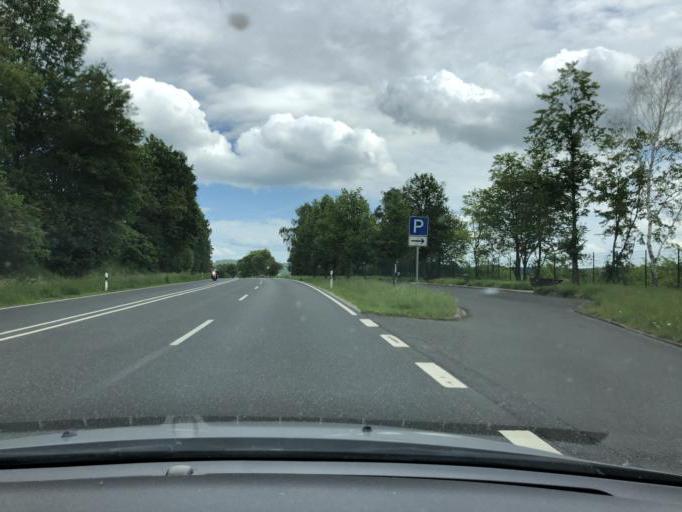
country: DE
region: Hesse
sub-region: Regierungsbezirk Kassel
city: Sontra
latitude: 51.0614
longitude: 9.9138
